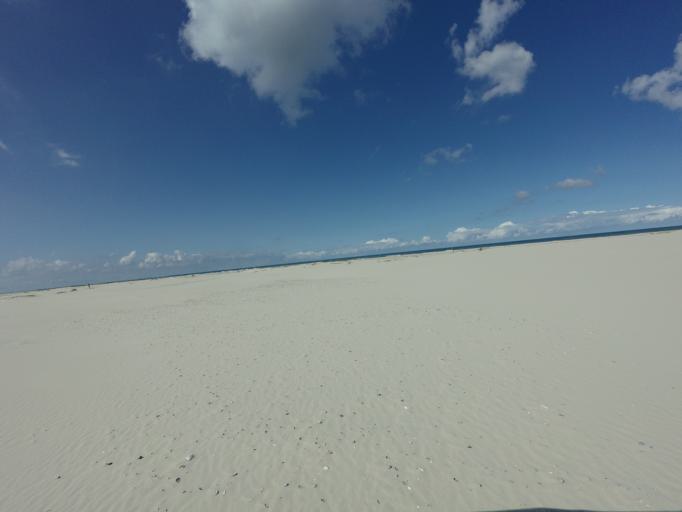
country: NL
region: Friesland
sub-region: Gemeente Terschelling
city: West-Terschelling
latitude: 53.3920
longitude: 5.2001
